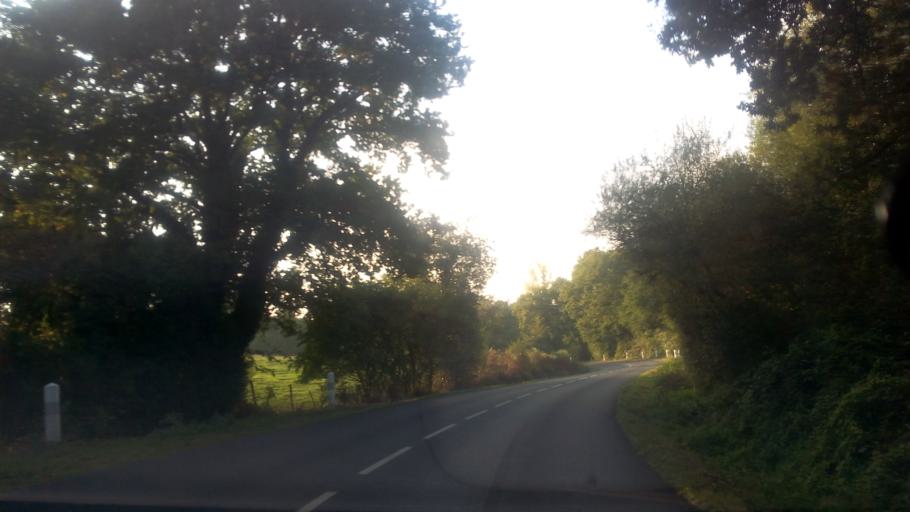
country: FR
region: Brittany
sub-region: Departement du Morbihan
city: Saint-Jean-la-Poterie
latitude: 47.6247
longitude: -2.1172
